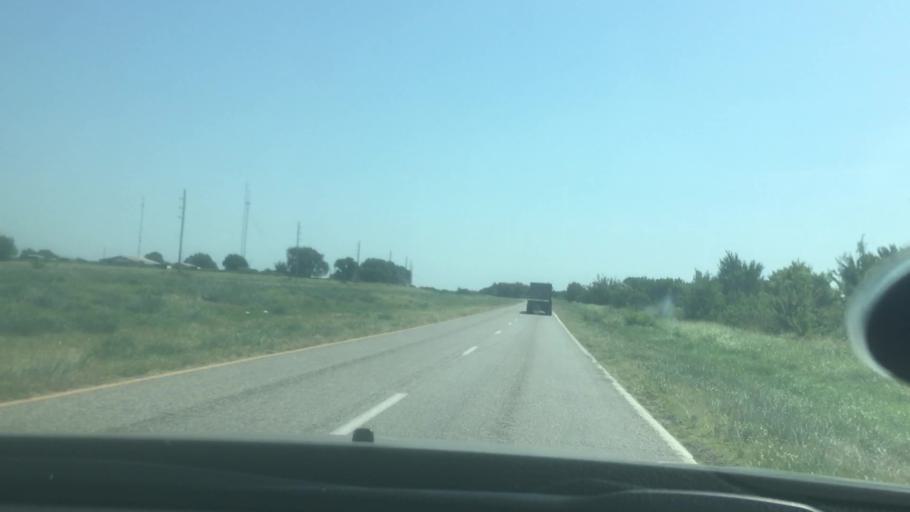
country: US
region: Oklahoma
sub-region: Pontotoc County
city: Ada
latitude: 34.7183
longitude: -96.7207
